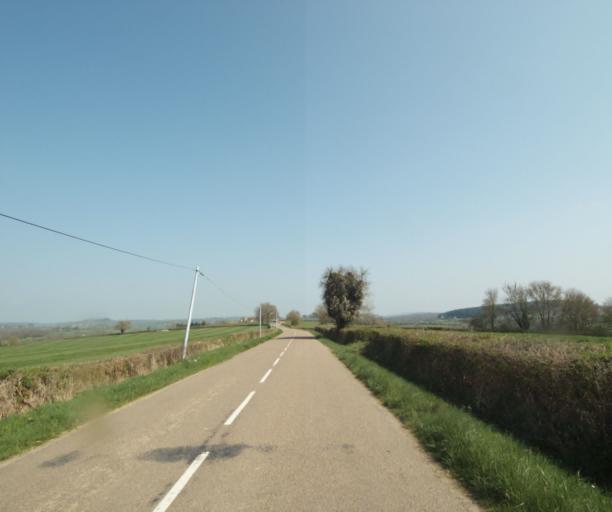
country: FR
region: Bourgogne
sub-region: Departement de Saone-et-Loire
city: Charolles
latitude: 46.4892
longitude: 4.3459
